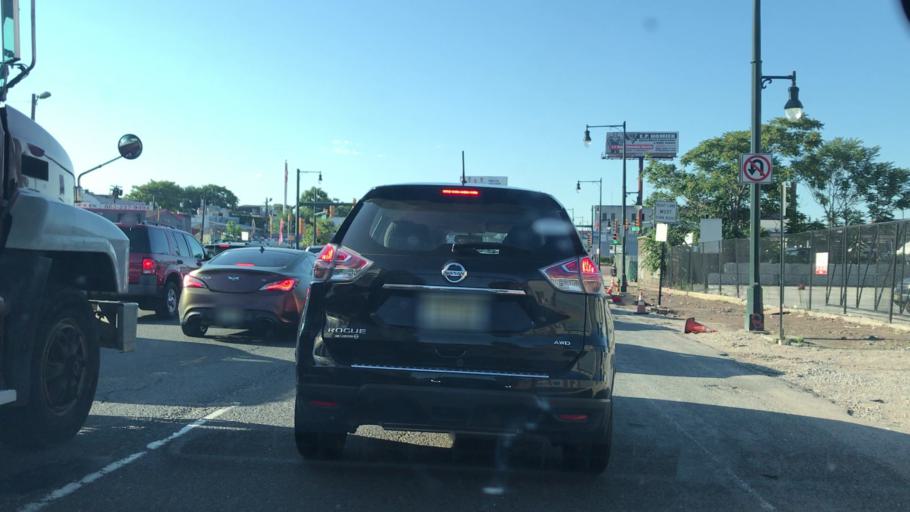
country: US
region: New Jersey
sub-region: Hudson County
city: East Newark
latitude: 40.7495
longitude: -74.1676
